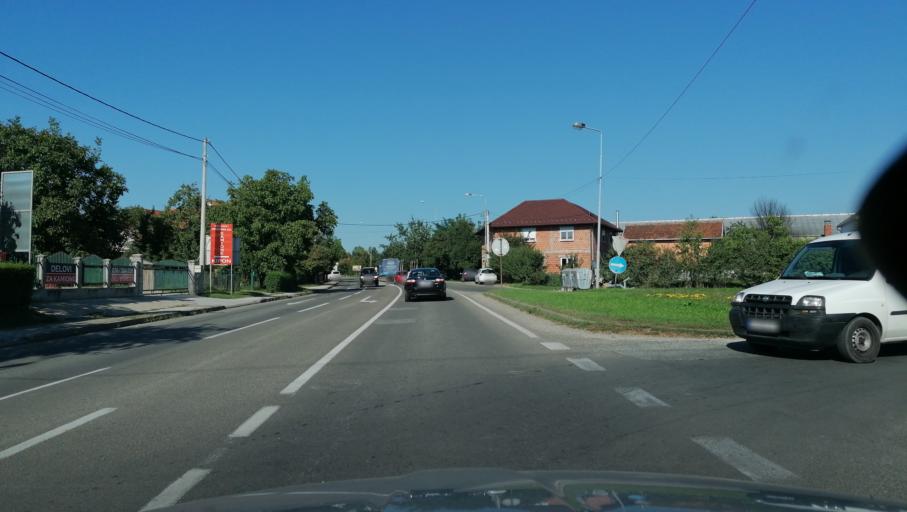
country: RS
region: Central Serbia
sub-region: Raski Okrug
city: Kraljevo
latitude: 43.7228
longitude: 20.6459
